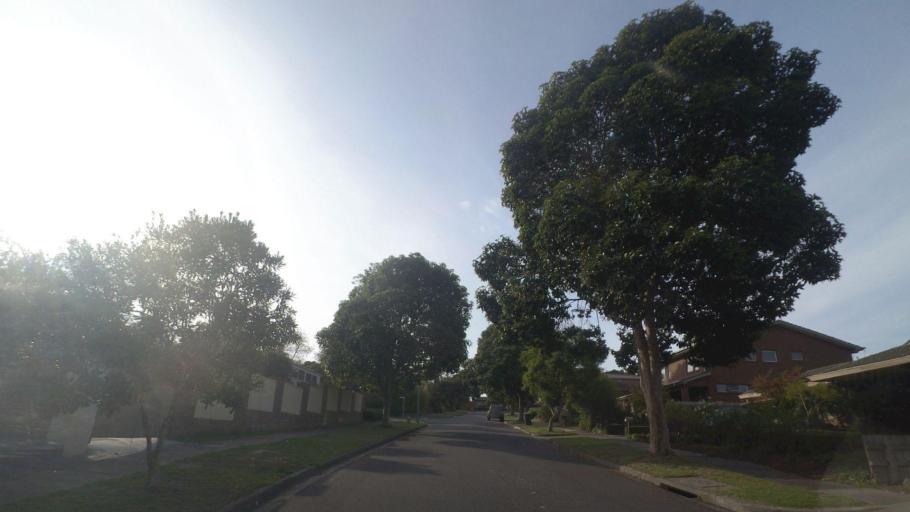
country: AU
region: Victoria
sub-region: Manningham
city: Doncaster East
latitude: -37.7769
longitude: 145.1543
